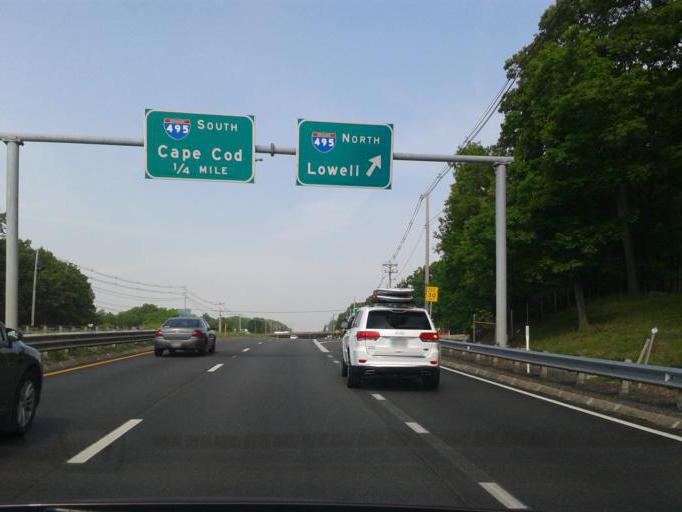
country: US
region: Massachusetts
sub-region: Worcester County
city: Southborough
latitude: 42.2889
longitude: -71.5615
